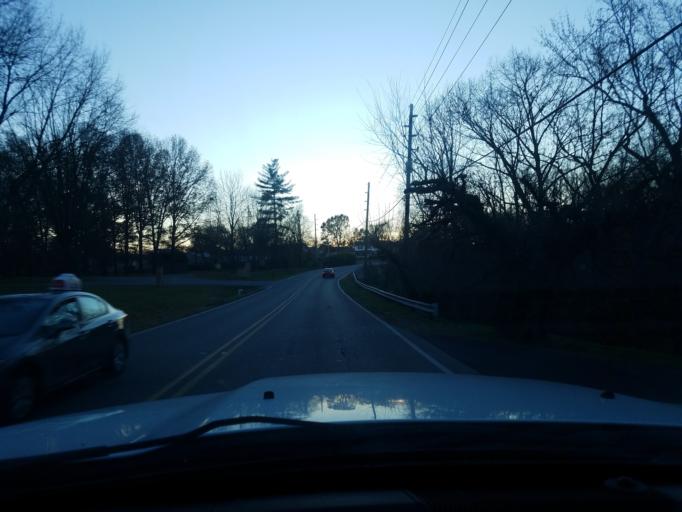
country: US
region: Indiana
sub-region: Floyd County
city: New Albany
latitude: 38.3322
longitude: -85.8096
